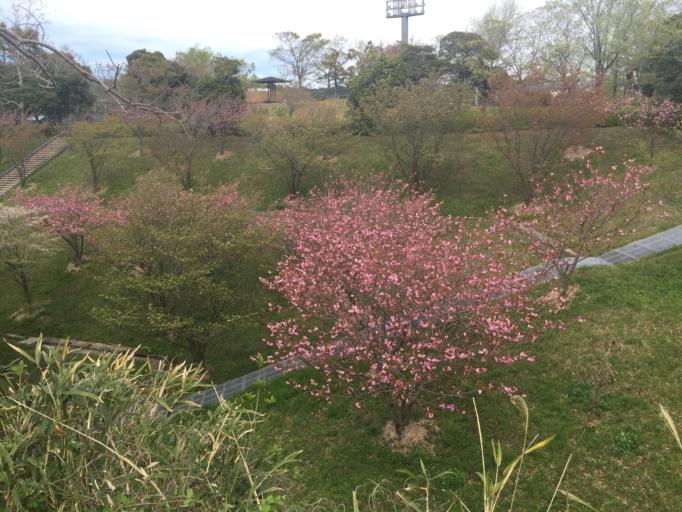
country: JP
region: Shizuoka
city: Kakegawa
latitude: 34.7894
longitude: 138.0411
